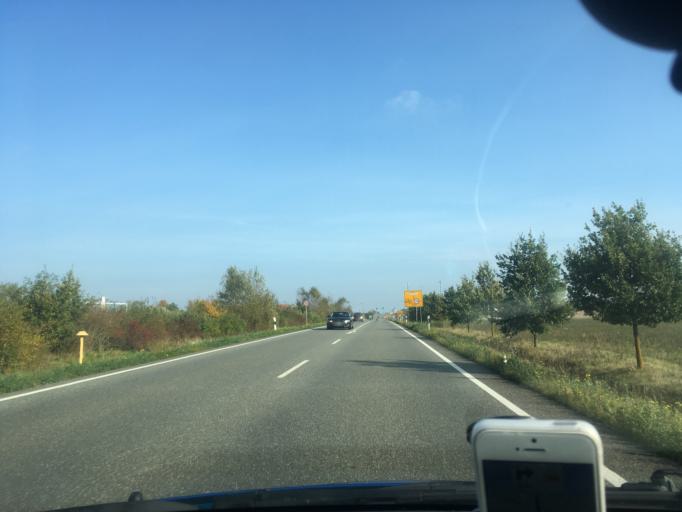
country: DE
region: Mecklenburg-Vorpommern
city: Klein Rogahn
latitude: 53.5624
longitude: 11.3601
